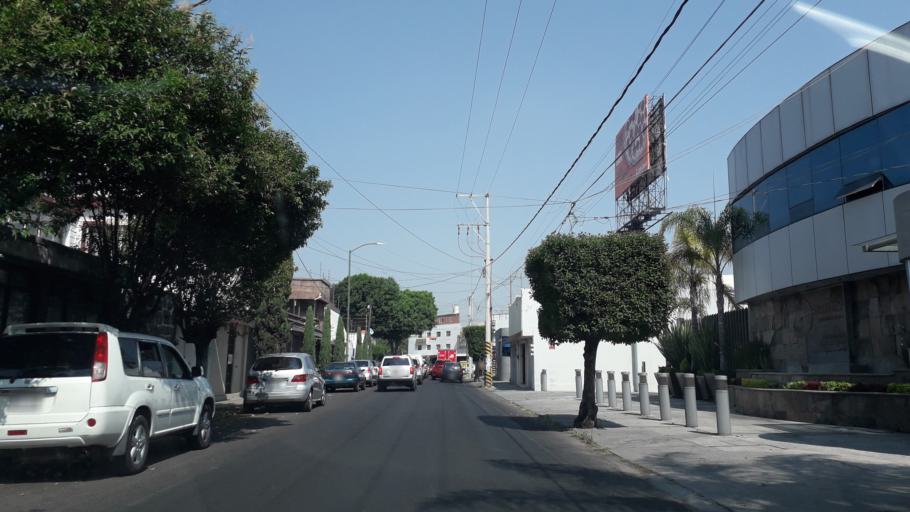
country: MX
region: Puebla
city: Puebla
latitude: 19.0347
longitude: -98.2134
